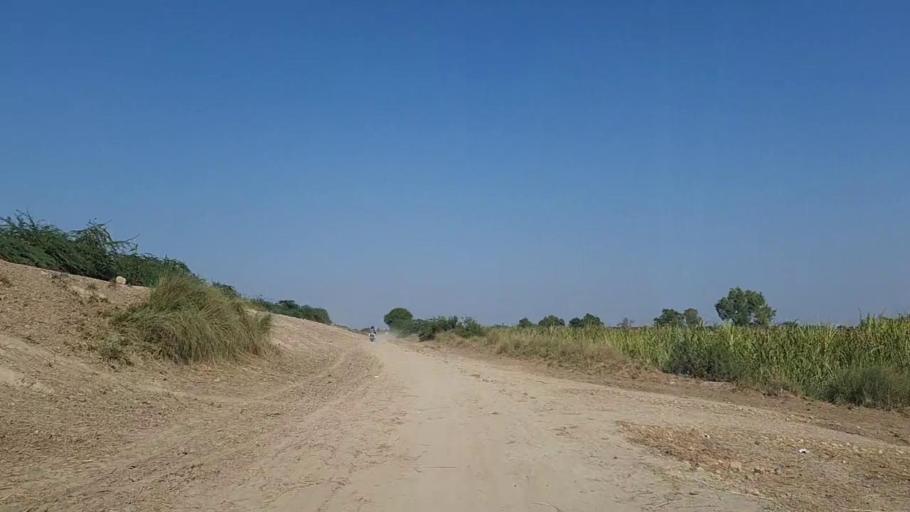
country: PK
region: Sindh
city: Thatta
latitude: 24.5854
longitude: 68.0374
